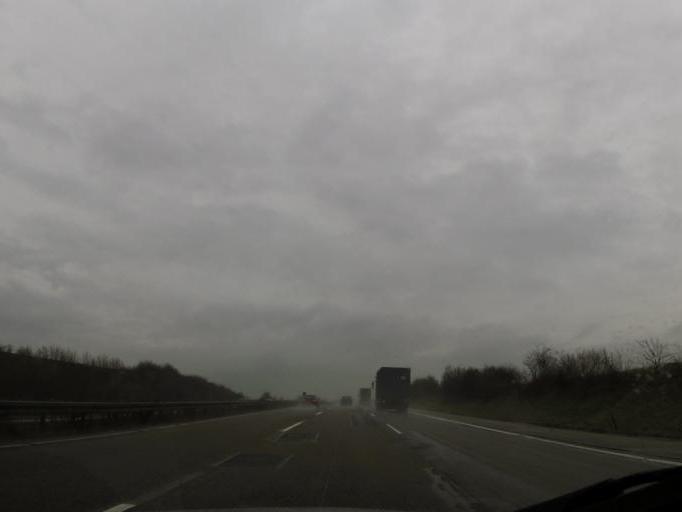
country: DE
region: Hesse
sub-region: Regierungsbezirk Giessen
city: Villmar
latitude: 50.3393
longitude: 8.1830
